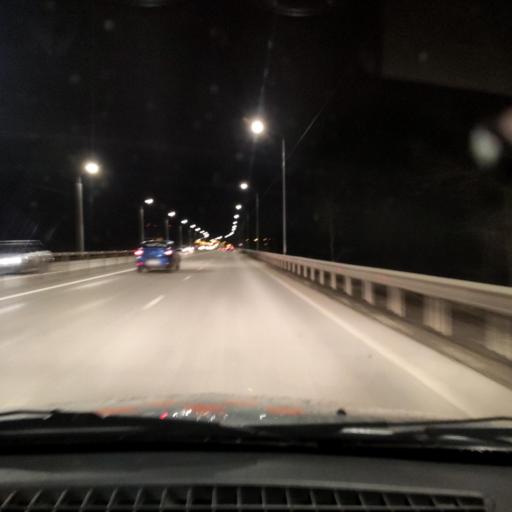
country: RU
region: Bashkortostan
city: Ufa
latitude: 54.6984
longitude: 55.8867
